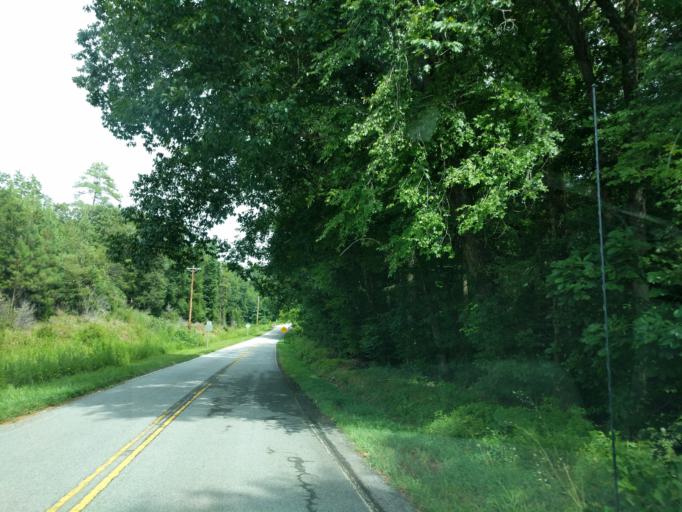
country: US
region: South Carolina
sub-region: Abbeville County
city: Lake Secession
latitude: 34.1975
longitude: -82.6133
